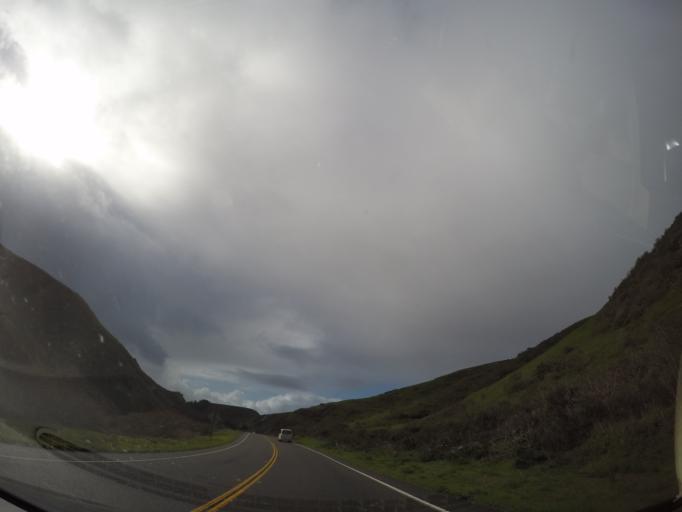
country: US
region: California
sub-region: Sonoma County
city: Bodega Bay
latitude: 38.3268
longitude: -123.0067
